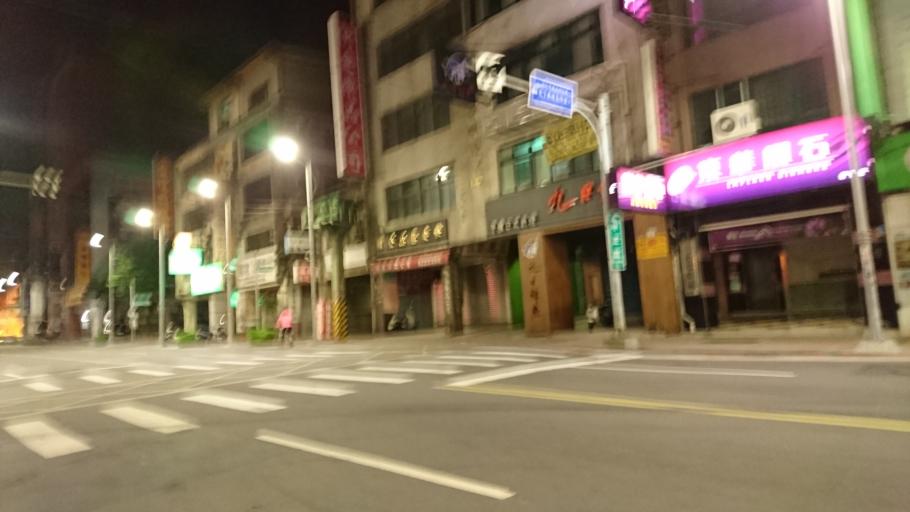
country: TW
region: Taiwan
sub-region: Hsinchu
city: Hsinchu
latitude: 24.8055
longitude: 120.9695
